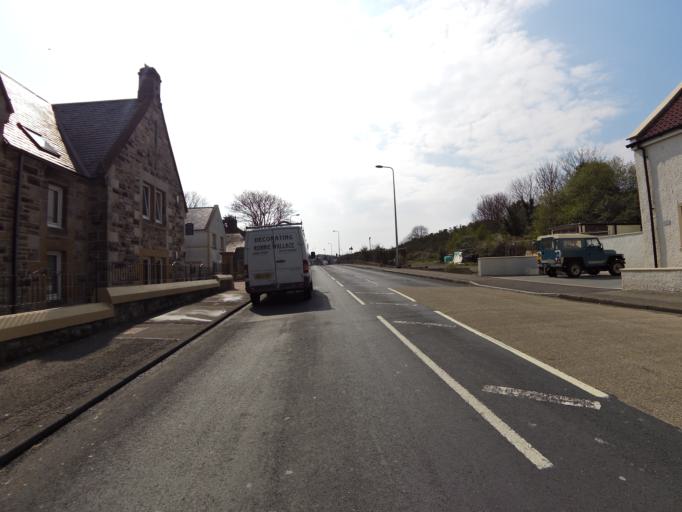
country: GB
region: Scotland
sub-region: Fife
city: Kinghorn
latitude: 56.0681
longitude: -3.1773
